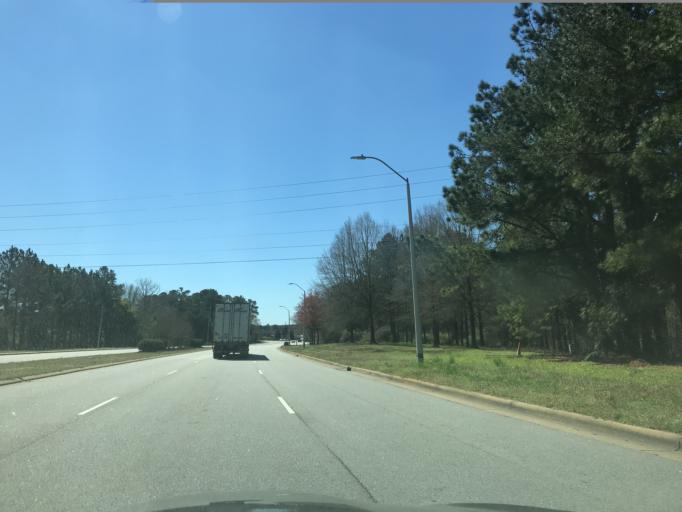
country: US
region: North Carolina
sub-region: Wake County
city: Garner
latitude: 35.7228
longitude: -78.6387
